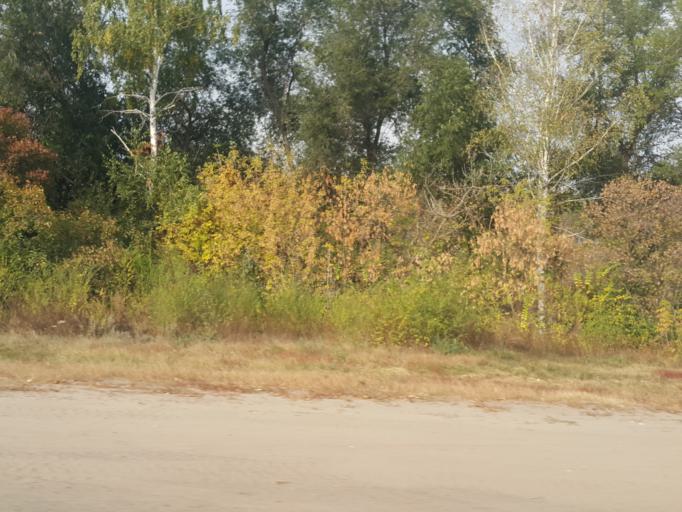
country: RU
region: Tambov
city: Bokino
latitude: 52.6672
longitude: 41.4511
